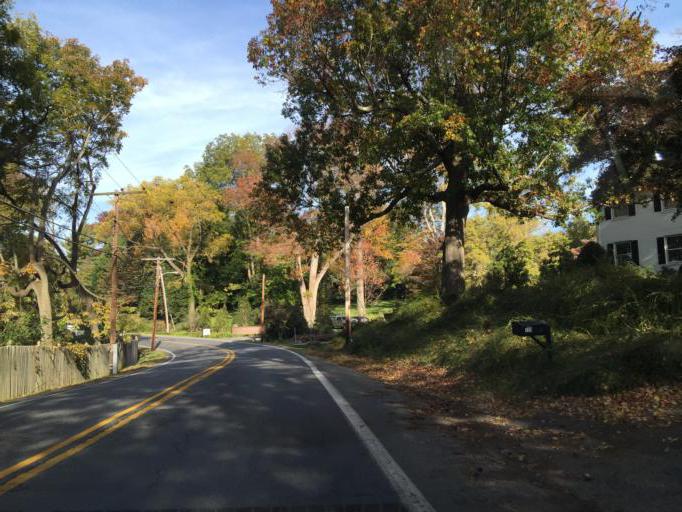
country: US
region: Maryland
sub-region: Baltimore County
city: Towson
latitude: 39.3839
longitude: -76.6299
